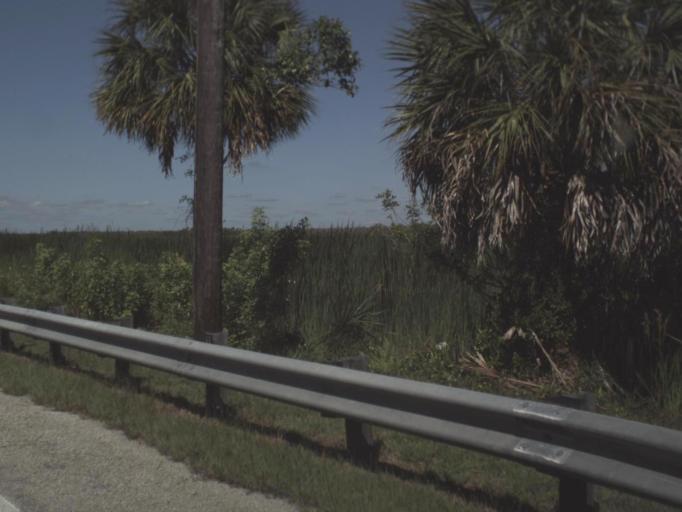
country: US
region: Florida
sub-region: Collier County
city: Marco
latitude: 25.9173
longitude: -81.3818
